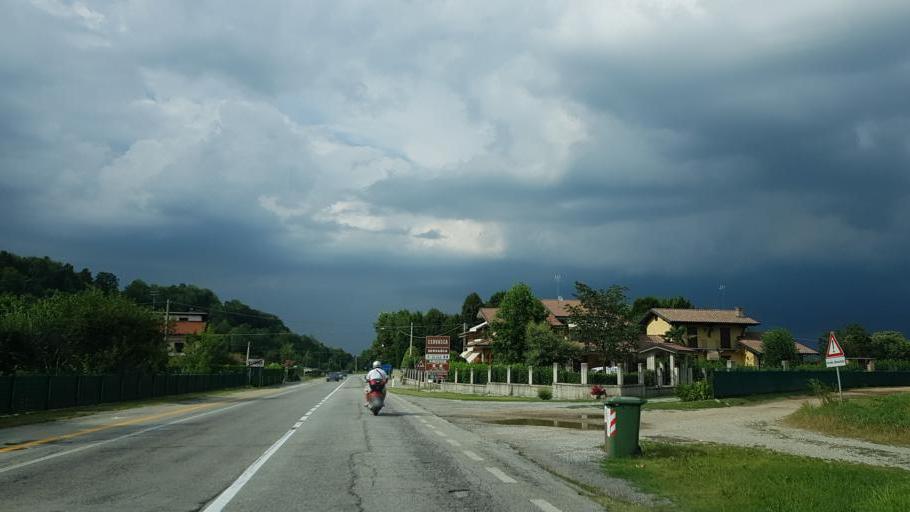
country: IT
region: Piedmont
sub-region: Provincia di Cuneo
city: Vignolo
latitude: 44.3690
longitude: 7.4744
